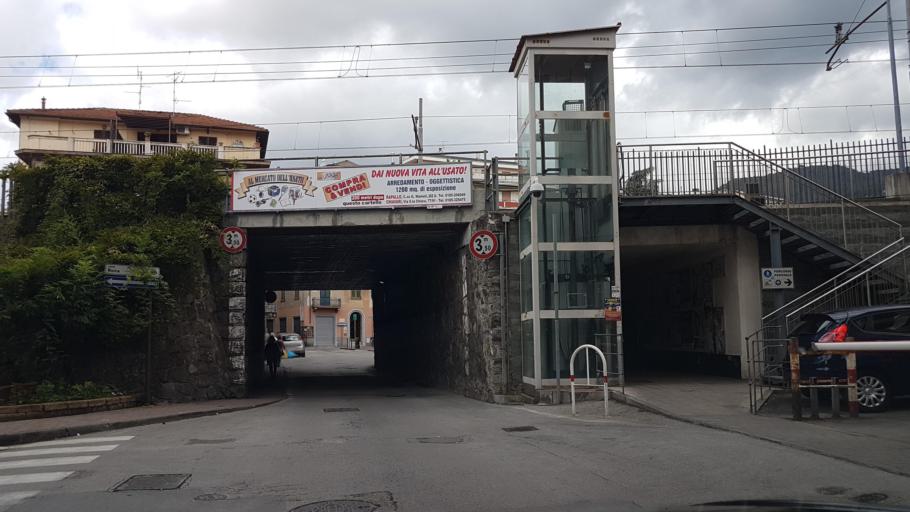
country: IT
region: Liguria
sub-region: Provincia di Genova
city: Rapallo
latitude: 44.3509
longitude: 9.2272
